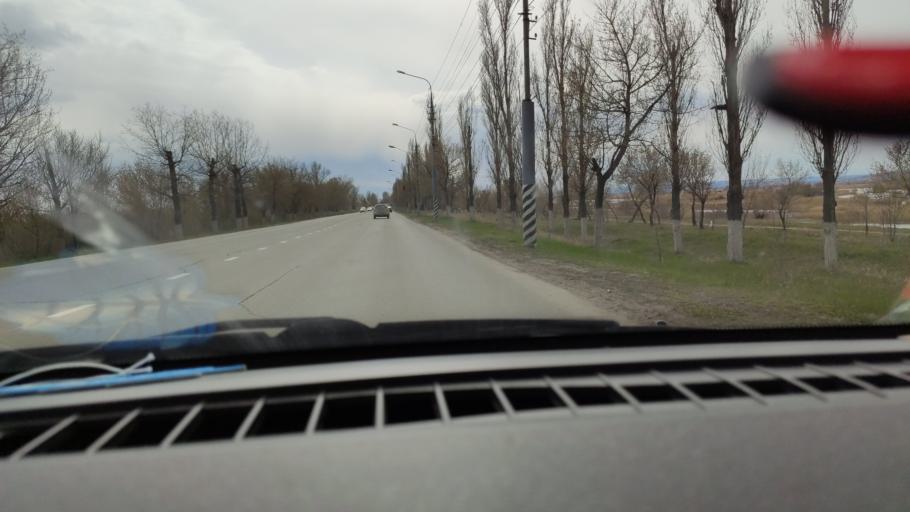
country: RU
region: Saratov
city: Privolzhskiy
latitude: 51.4373
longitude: 46.0628
